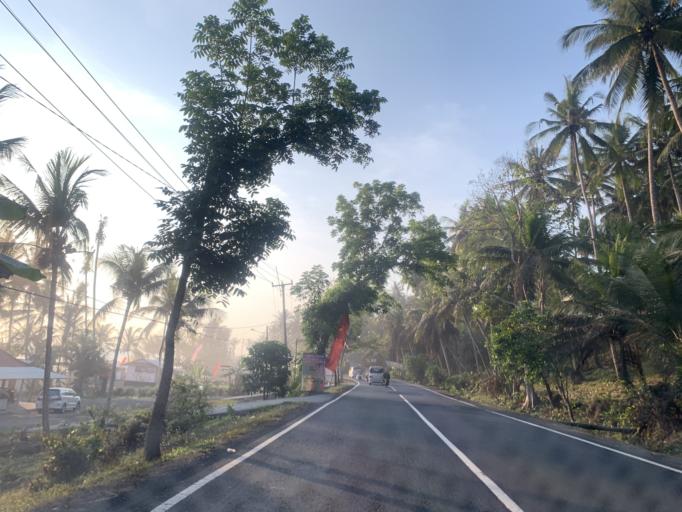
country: ID
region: Bali
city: Banjar Swastika
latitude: -8.4637
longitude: 114.9116
